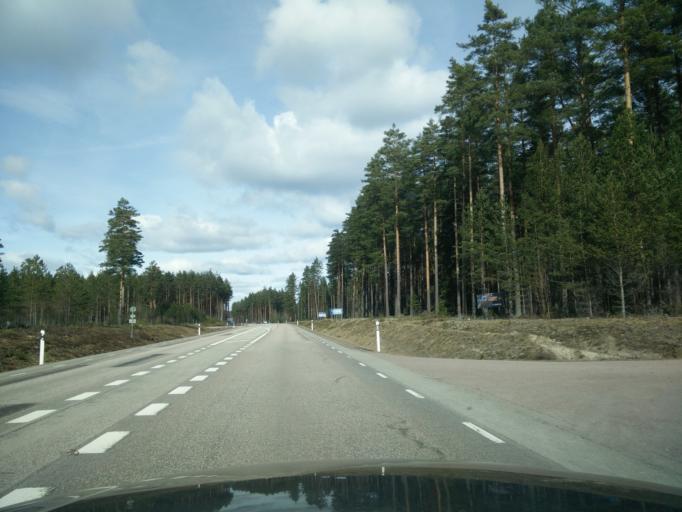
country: SE
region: Vaermland
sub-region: Hagfors Kommun
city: Hagfors
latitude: 60.0255
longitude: 13.5900
